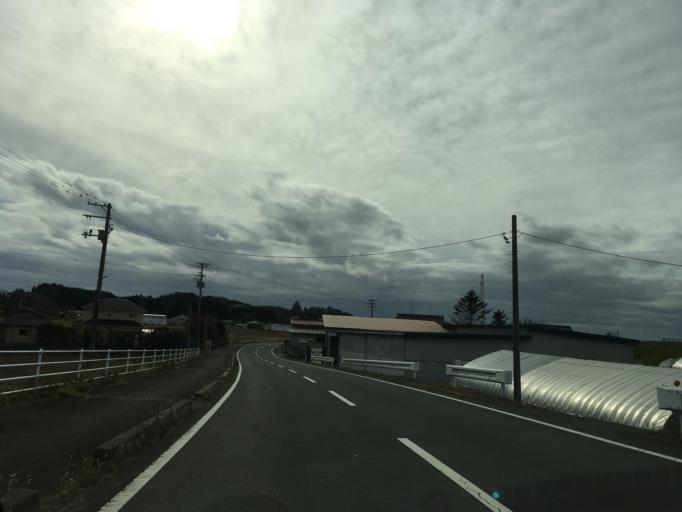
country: JP
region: Iwate
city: Ichinoseki
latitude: 38.7378
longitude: 141.2775
